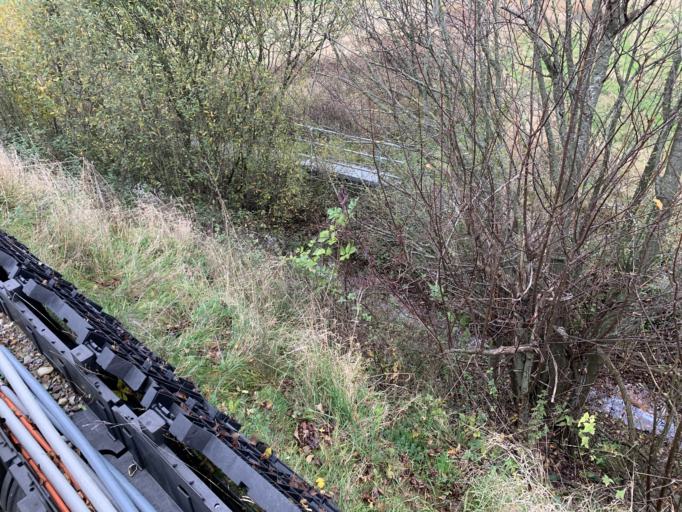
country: DK
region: Zealand
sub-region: Ringsted Kommune
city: Ringsted
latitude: 55.4286
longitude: 11.7603
